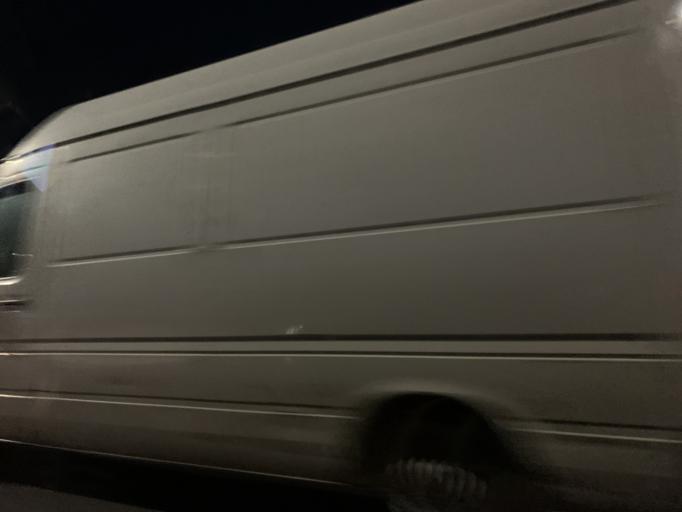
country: ES
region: Extremadura
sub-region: Provincia de Badajoz
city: Badajoz
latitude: 38.8802
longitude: -6.9404
